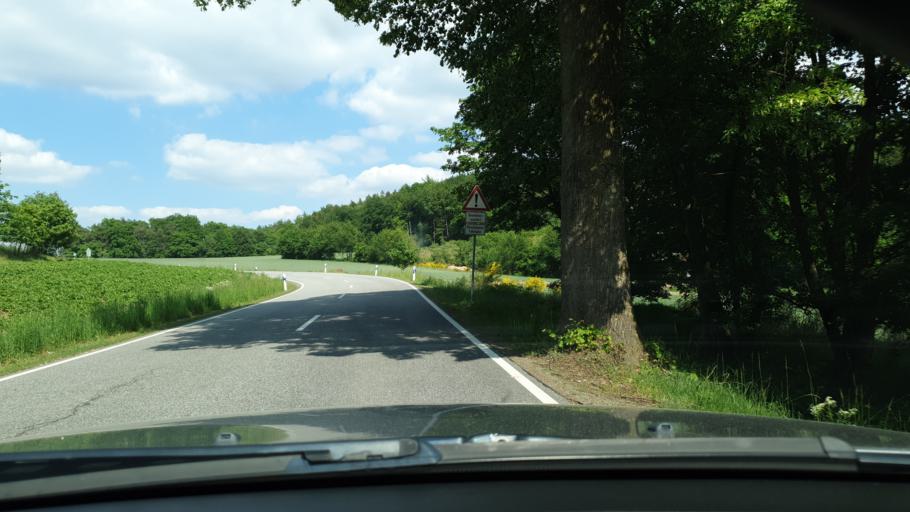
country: DE
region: Rheinland-Pfalz
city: Lambsborn
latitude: 49.3724
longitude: 7.4421
